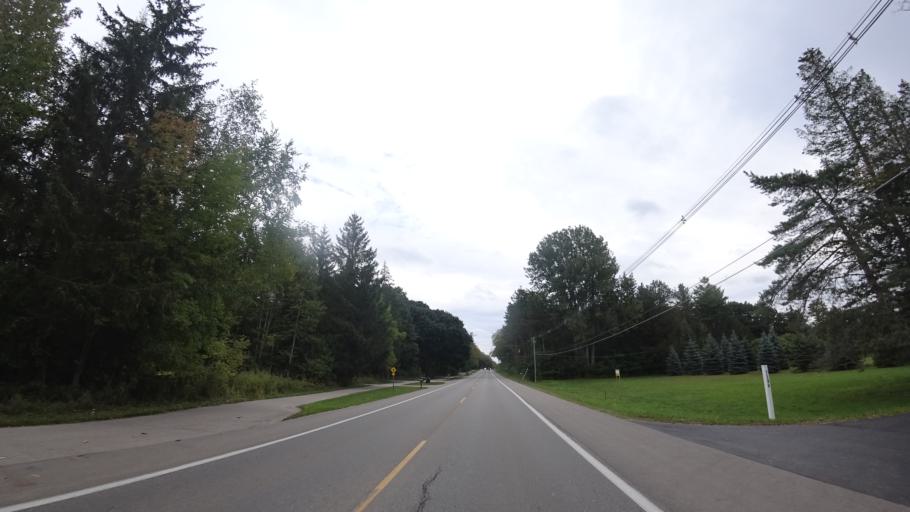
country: US
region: Michigan
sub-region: Emmet County
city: Harbor Springs
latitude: 45.4308
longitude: -84.9320
